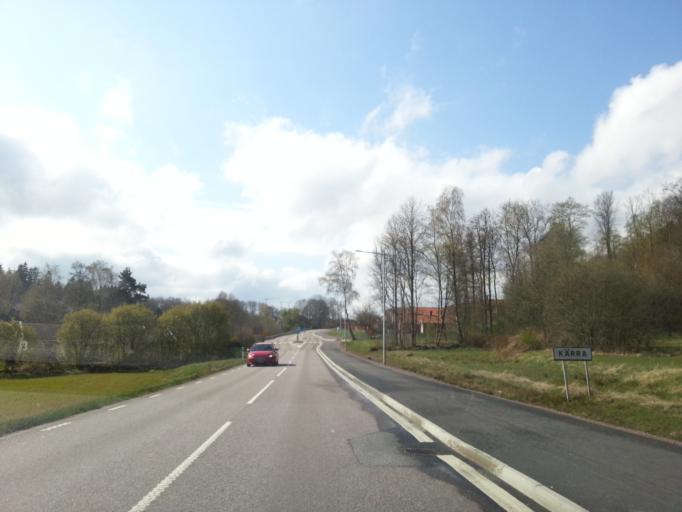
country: SE
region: Vaestra Goetaland
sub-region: Ale Kommun
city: Surte
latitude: 57.8071
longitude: 11.9971
